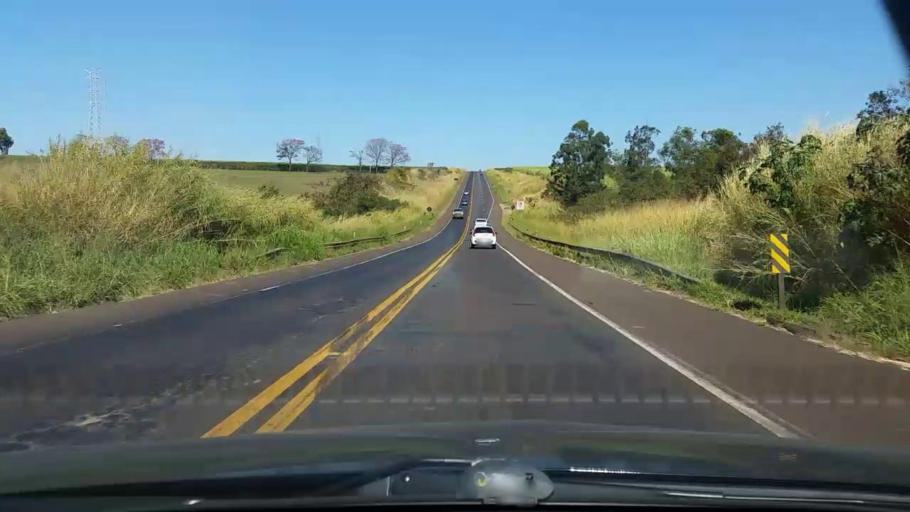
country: BR
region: Sao Paulo
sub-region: Jau
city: Jau
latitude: -22.3477
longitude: -48.5724
